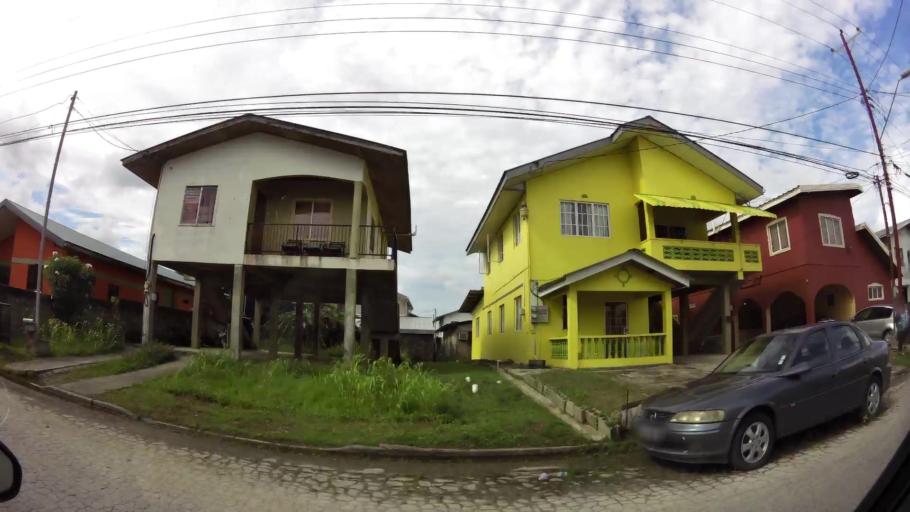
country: TT
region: Chaguanas
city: Chaguanas
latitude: 10.5072
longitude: -61.3972
